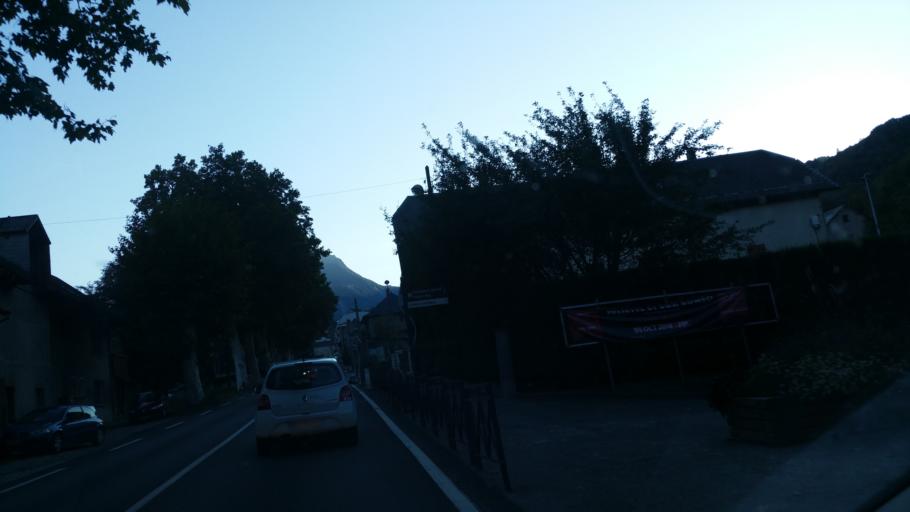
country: FR
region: Rhone-Alpes
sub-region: Departement de la Savoie
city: Saint-Jean-de-Maurienne
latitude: 45.2816
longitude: 6.3473
